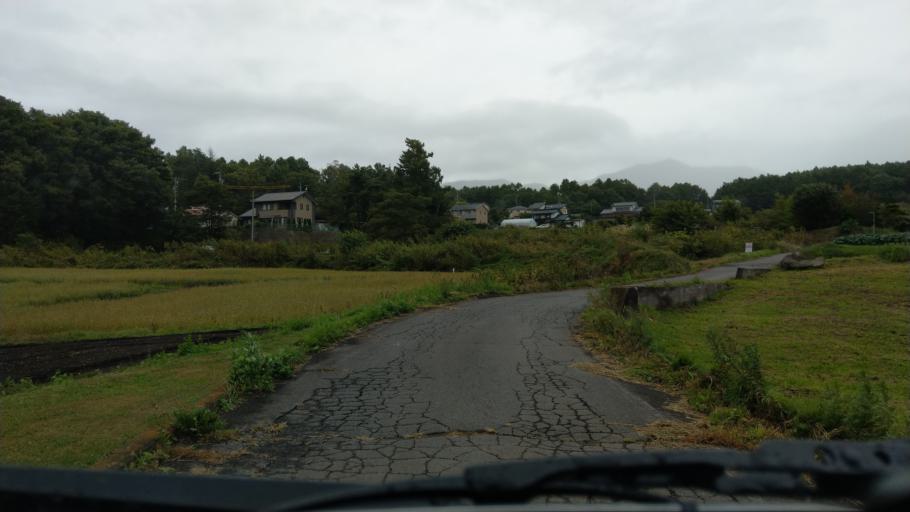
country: JP
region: Nagano
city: Komoro
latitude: 36.3359
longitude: 138.4524
